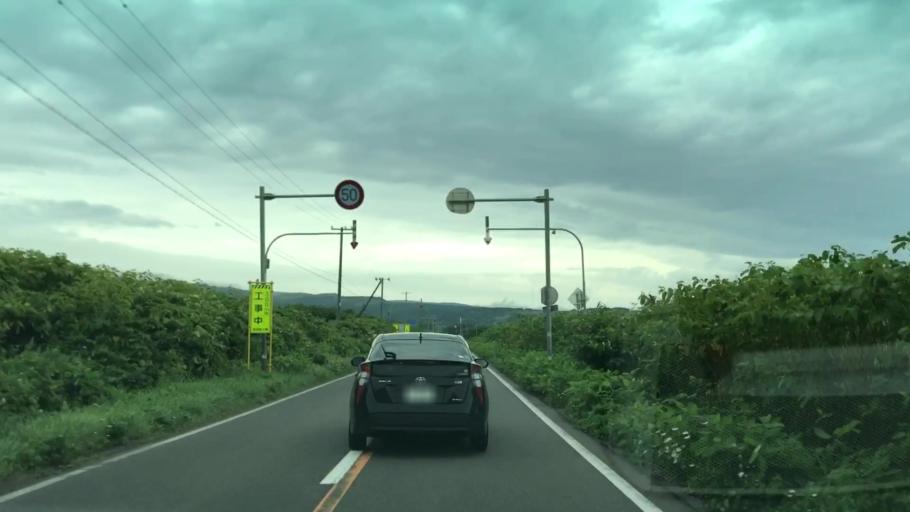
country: JP
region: Hokkaido
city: Iwanai
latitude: 42.8947
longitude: 140.3771
